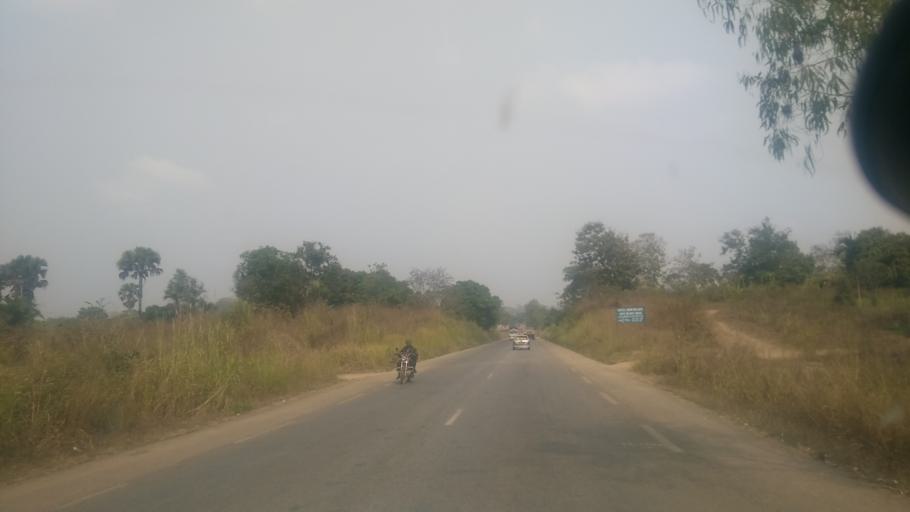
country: CM
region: Centre
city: Bafia
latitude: 4.7257
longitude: 11.2253
